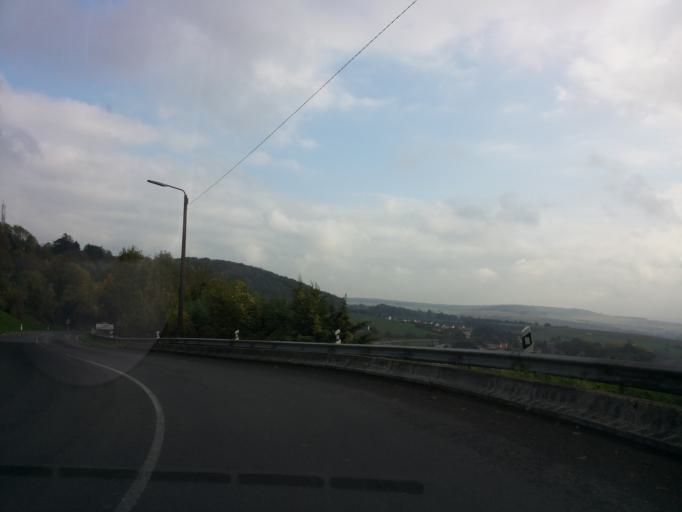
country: FR
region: Lorraine
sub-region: Departement de la Meuse
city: Montmedy
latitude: 49.5226
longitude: 5.3618
